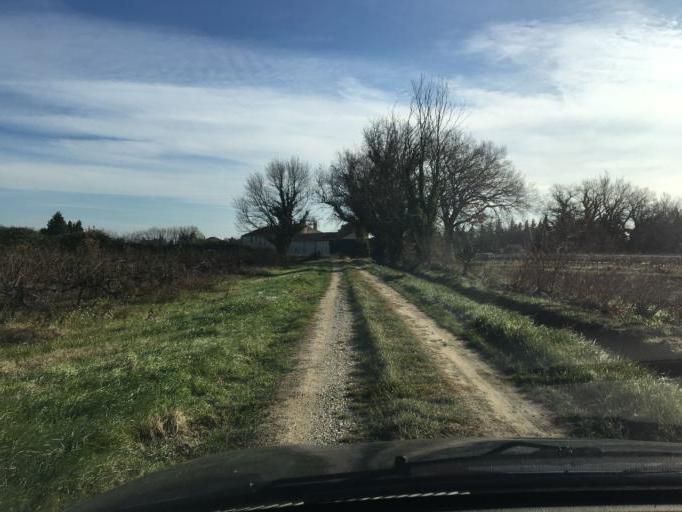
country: FR
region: Provence-Alpes-Cote d'Azur
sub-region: Departement du Vaucluse
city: Jonquieres
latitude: 44.1414
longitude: 4.9008
